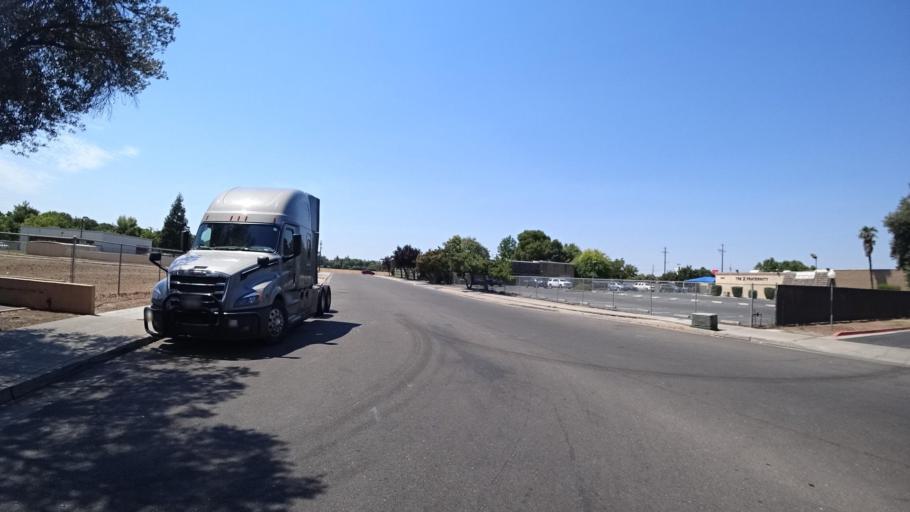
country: US
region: California
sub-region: Fresno County
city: Sunnyside
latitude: 36.7374
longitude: -119.6931
